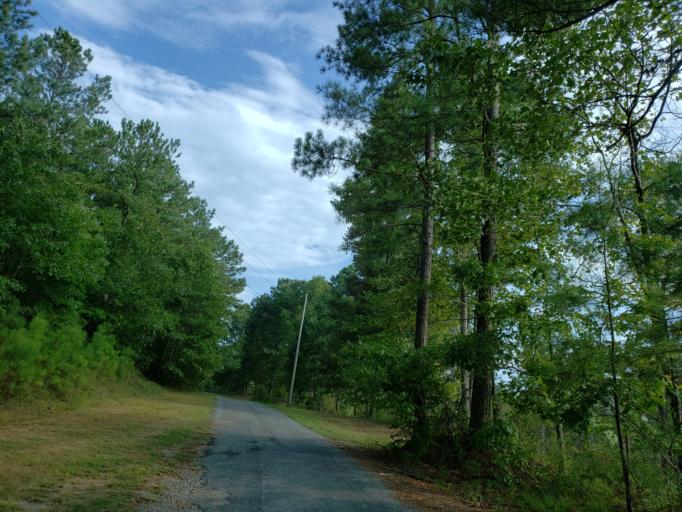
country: US
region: Georgia
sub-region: Bartow County
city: Emerson
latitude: 34.1939
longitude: -84.6498
